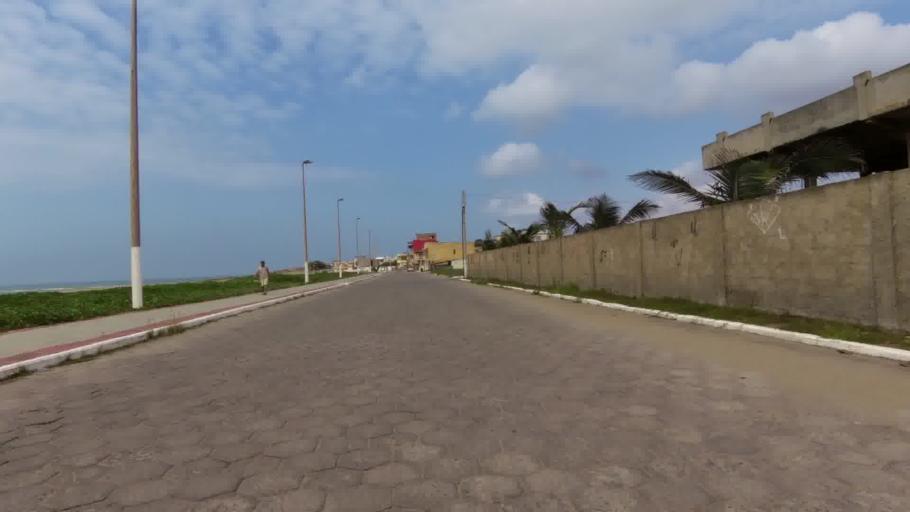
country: BR
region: Espirito Santo
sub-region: Marataizes
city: Marataizes
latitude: -21.0296
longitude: -40.8126
